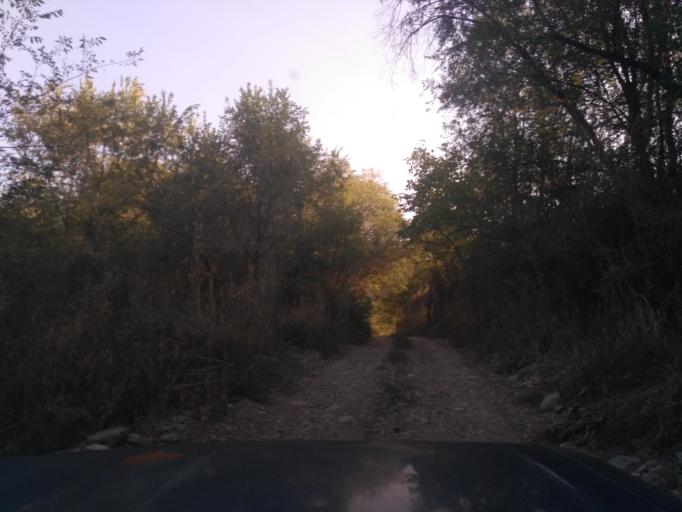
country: KZ
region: Almaty Oblysy
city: Burunday
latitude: 43.1536
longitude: 76.3710
